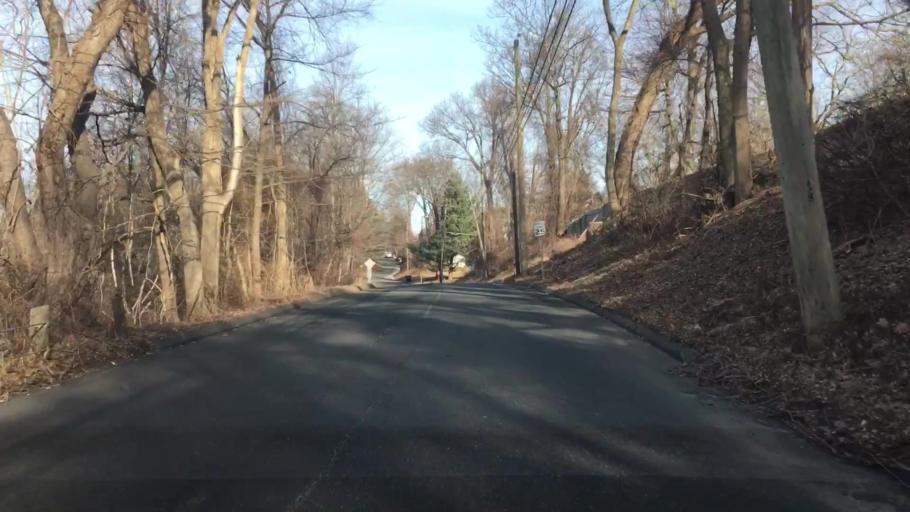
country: US
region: Connecticut
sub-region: Fairfield County
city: Danbury
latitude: 41.3712
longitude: -73.5042
